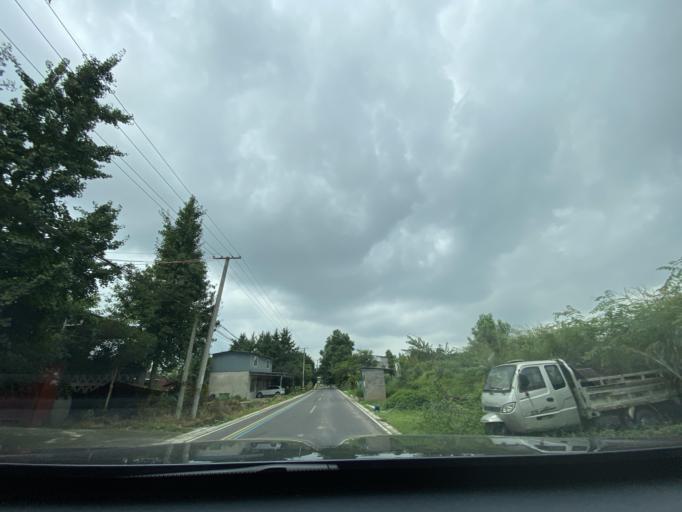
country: CN
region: Sichuan
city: Dongsheng
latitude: 30.4080
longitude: 104.0001
